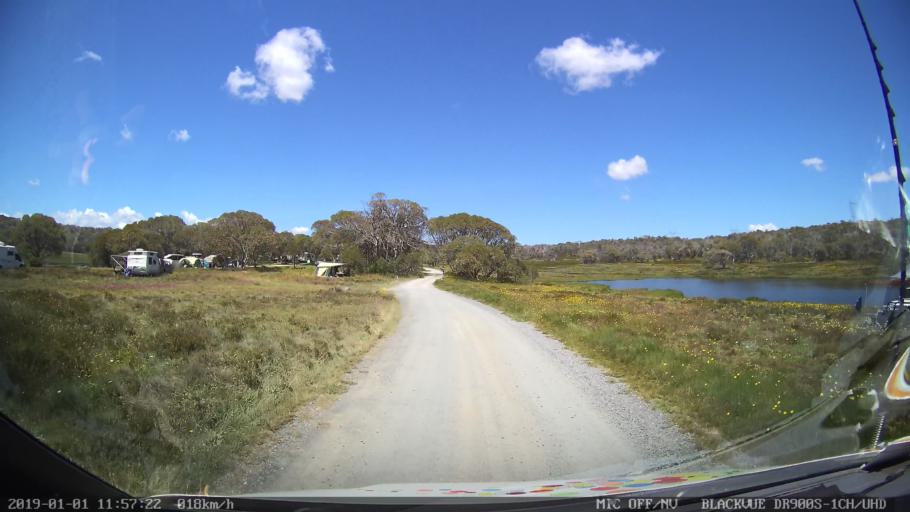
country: AU
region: New South Wales
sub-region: Snowy River
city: Jindabyne
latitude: -35.8875
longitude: 148.4492
